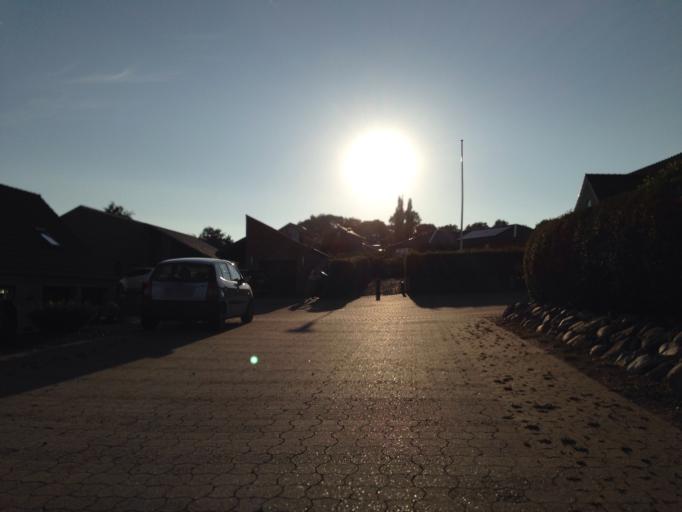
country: DK
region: South Denmark
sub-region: Middelfart Kommune
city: Norre Aby
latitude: 55.4859
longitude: 9.9161
